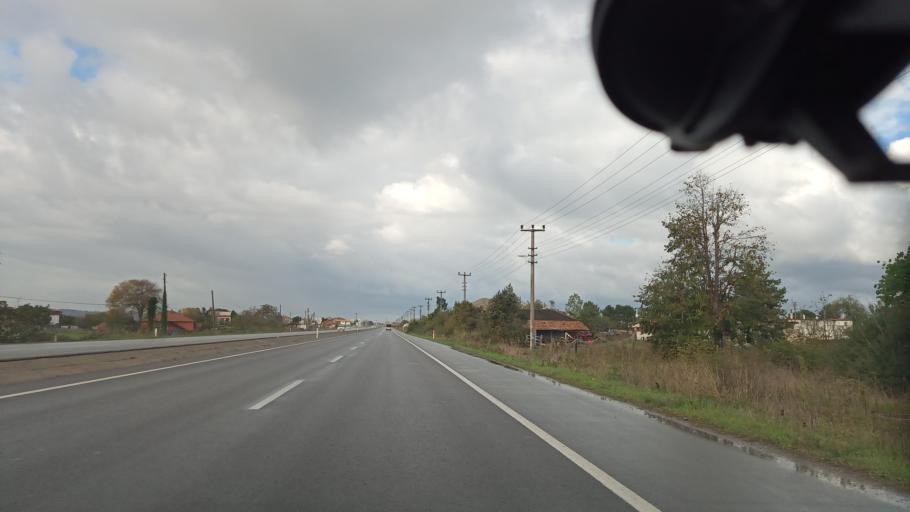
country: TR
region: Sakarya
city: Karasu
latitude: 41.0784
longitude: 30.7757
